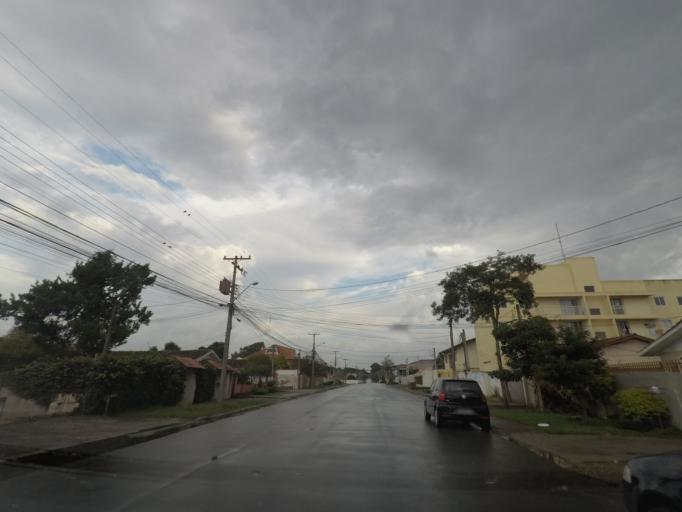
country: BR
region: Parana
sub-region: Sao Jose Dos Pinhais
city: Sao Jose dos Pinhais
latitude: -25.4908
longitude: -49.2482
